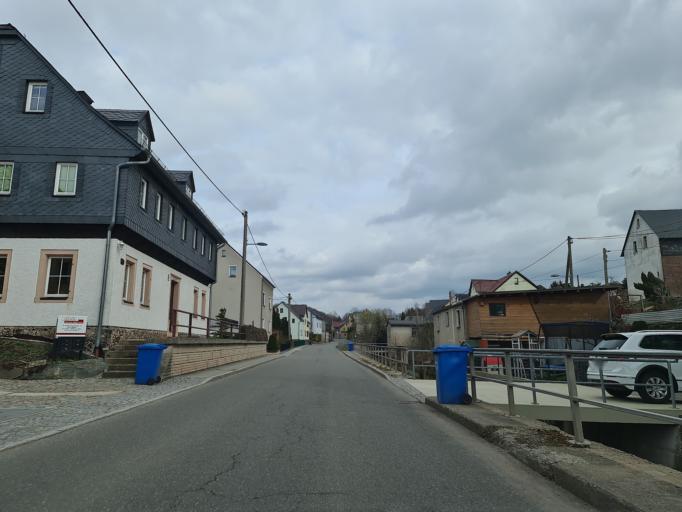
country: DE
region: Saxony
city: Reinsdorf
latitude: 50.7128
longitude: 12.6074
